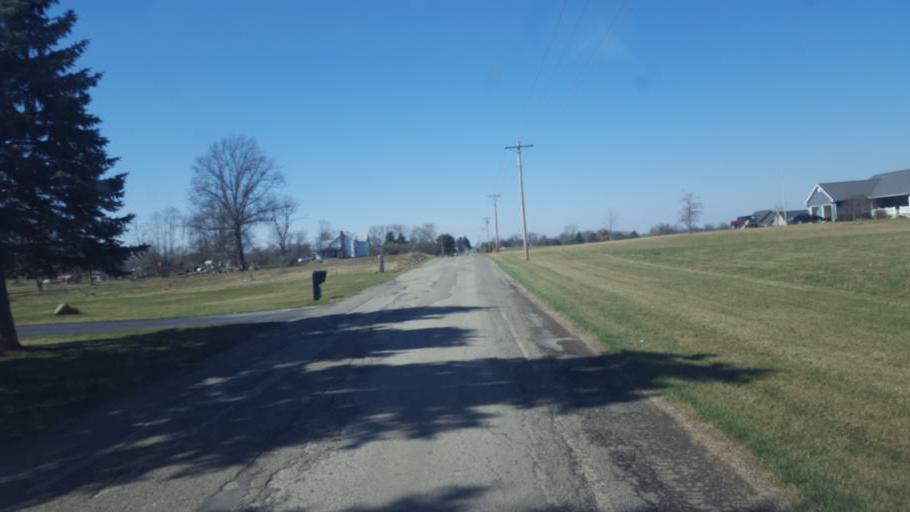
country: US
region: Ohio
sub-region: Morrow County
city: Mount Gilead
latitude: 40.5158
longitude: -82.8114
